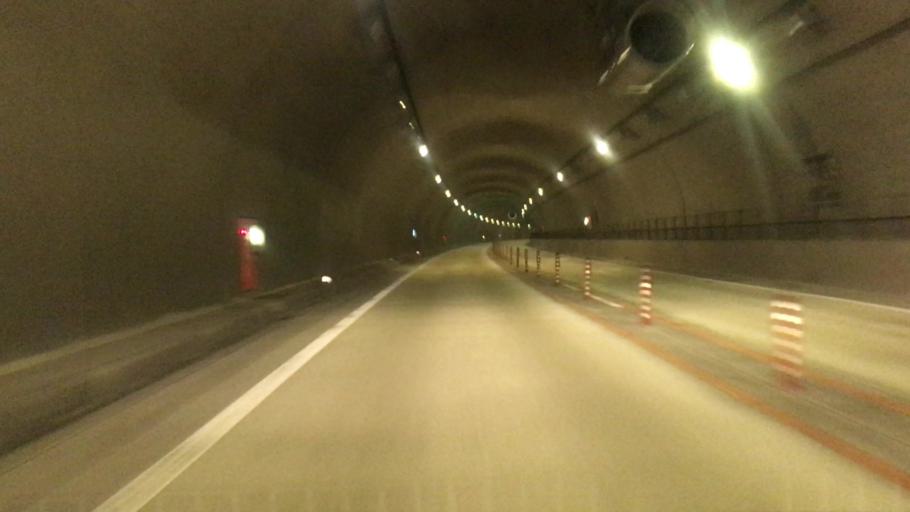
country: JP
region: Hyogo
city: Toyooka
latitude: 35.3469
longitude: 134.7800
